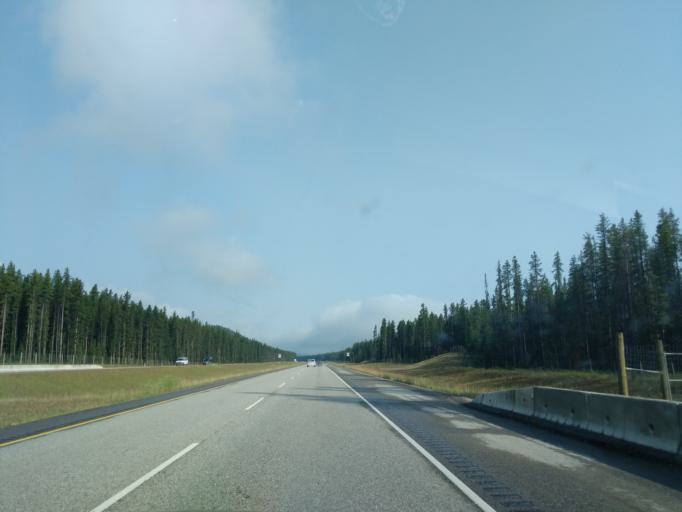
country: CA
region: Alberta
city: Lake Louise
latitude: 51.3360
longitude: -116.0598
